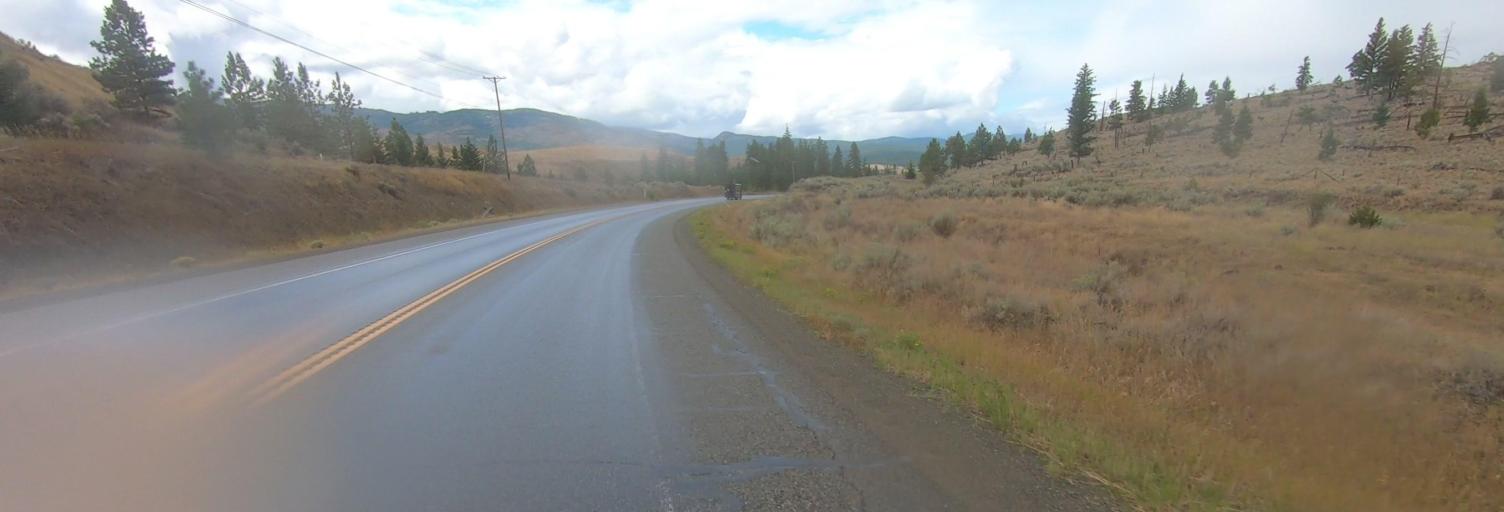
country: CA
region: British Columbia
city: Kamloops
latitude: 50.6610
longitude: -120.5325
